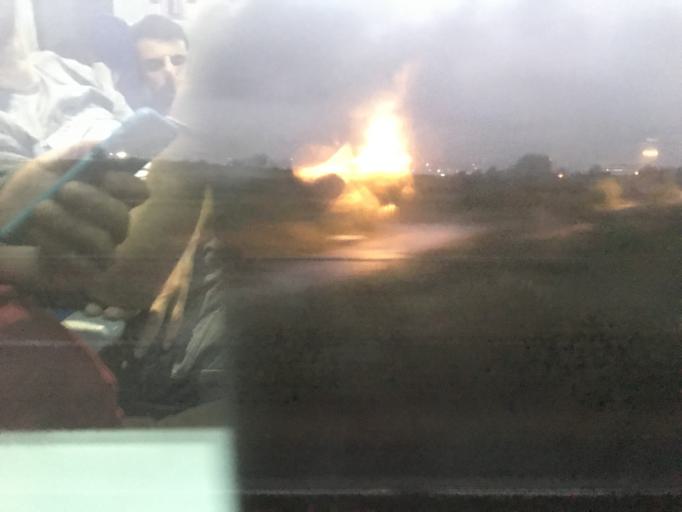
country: TR
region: Kocaeli
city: Derince
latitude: 40.7489
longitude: 29.7982
